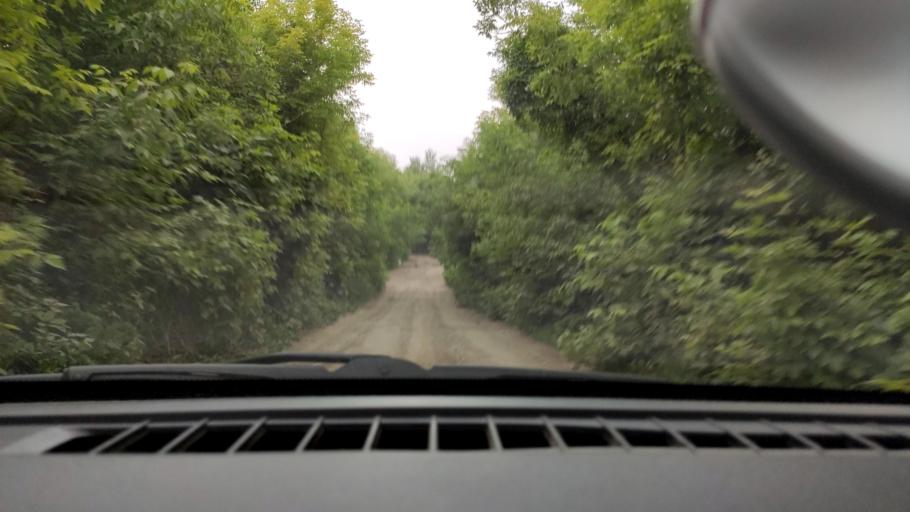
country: RU
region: Samara
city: Petra-Dubrava
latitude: 53.2773
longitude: 50.3239
